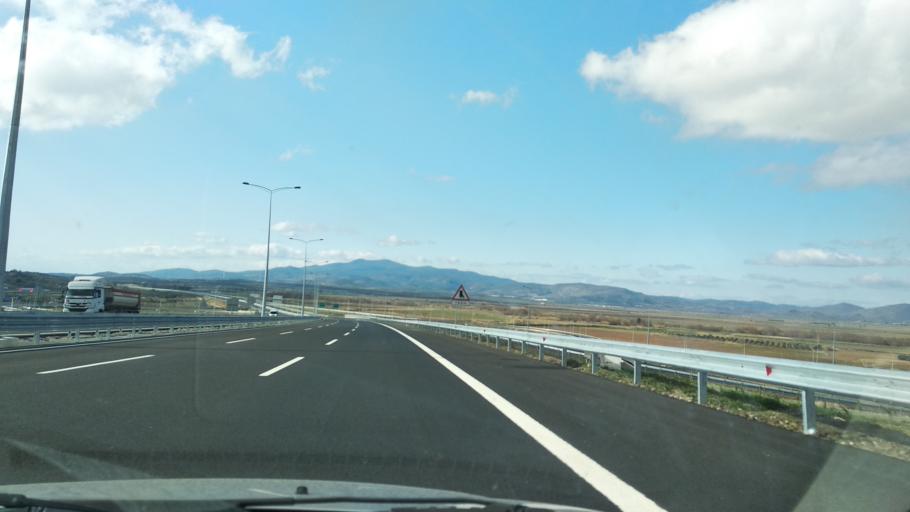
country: TR
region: Izmir
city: Zeytindag
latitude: 38.9736
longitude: 27.0489
